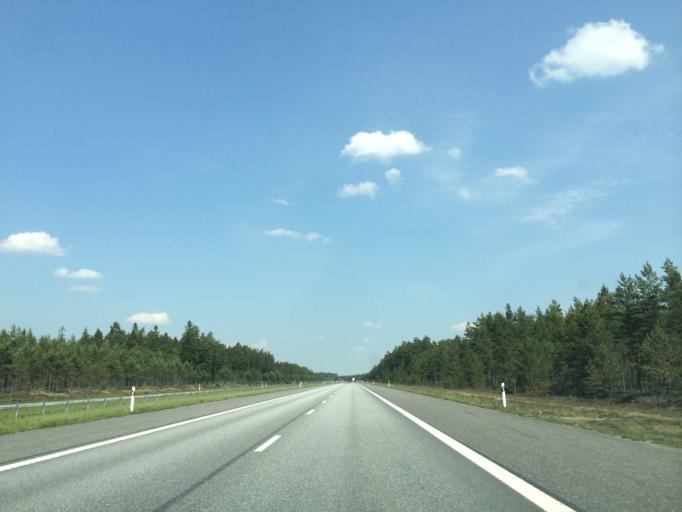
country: SE
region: Joenkoeping
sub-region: Vaggeryds Kommun
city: Skillingaryd
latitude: 57.3070
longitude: 14.0938
